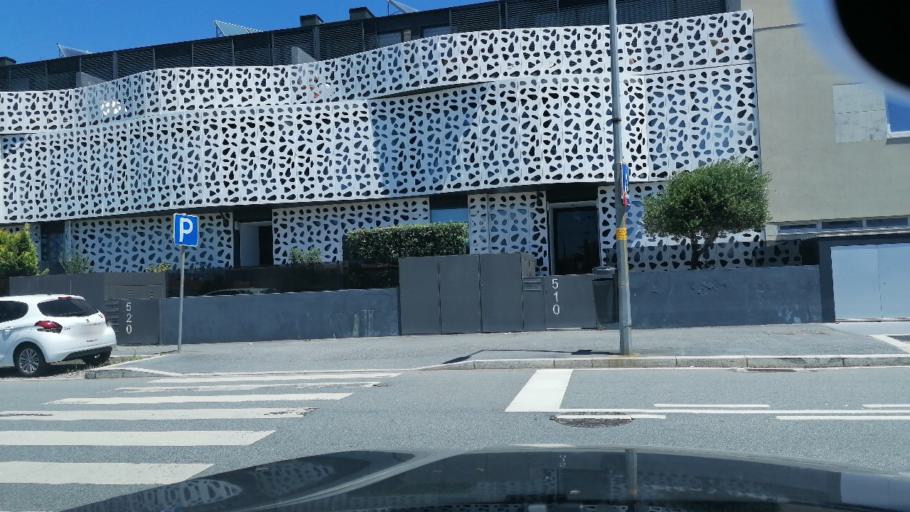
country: PT
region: Porto
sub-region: Matosinhos
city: Lavra
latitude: 41.2525
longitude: -8.7199
